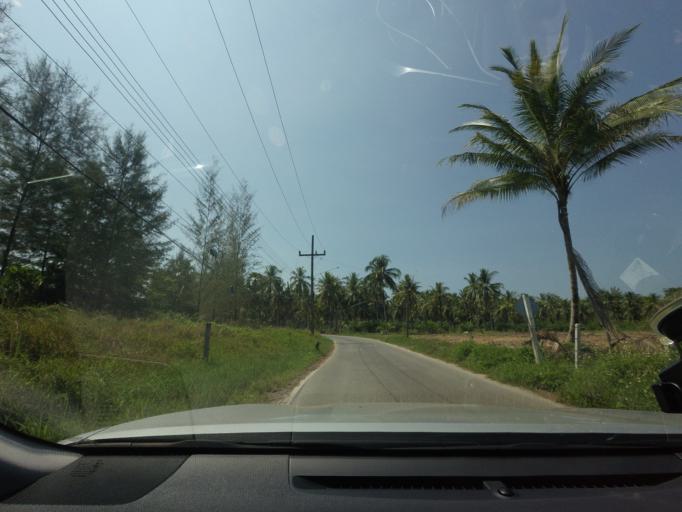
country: TH
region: Phangnga
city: Ban Khao Lak
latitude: 8.6972
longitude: 98.2473
